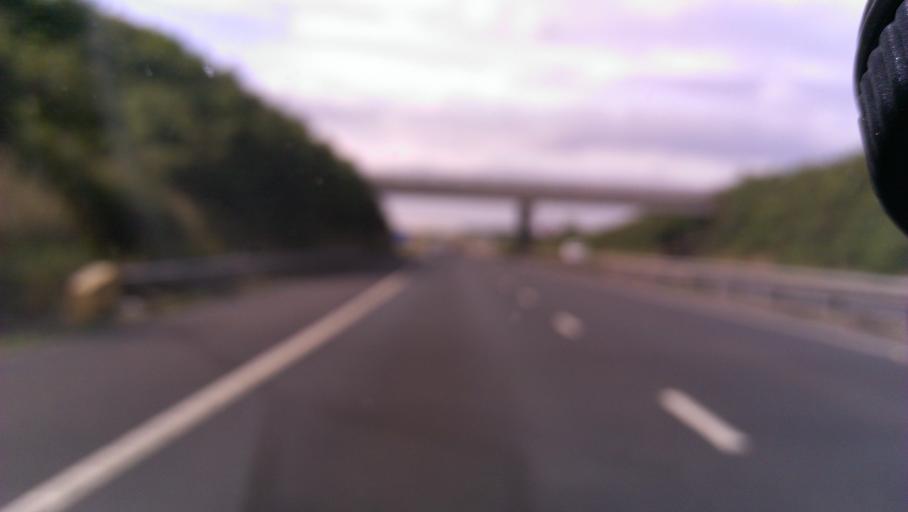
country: GB
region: England
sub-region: Cambridgeshire
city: Duxford
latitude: 52.0871
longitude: 0.1495
